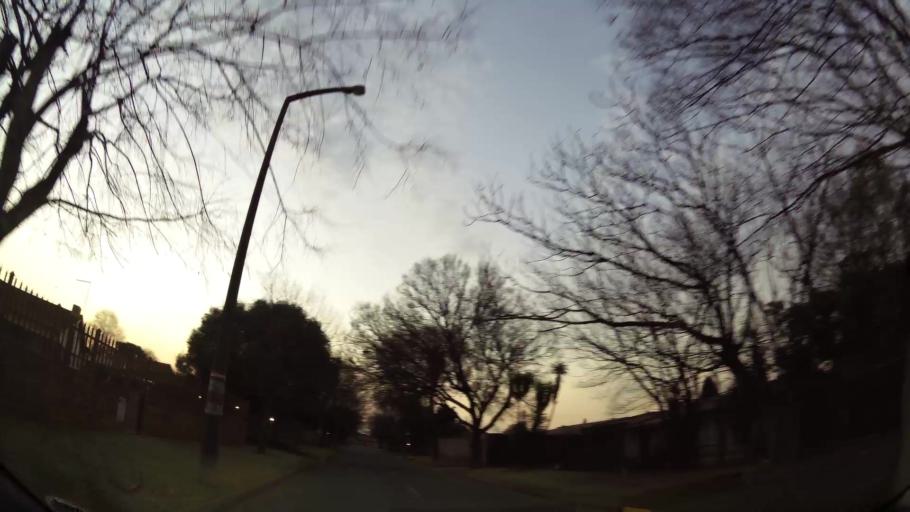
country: ZA
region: Gauteng
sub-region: Ekurhuleni Metropolitan Municipality
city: Benoni
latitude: -26.1441
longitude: 28.3095
